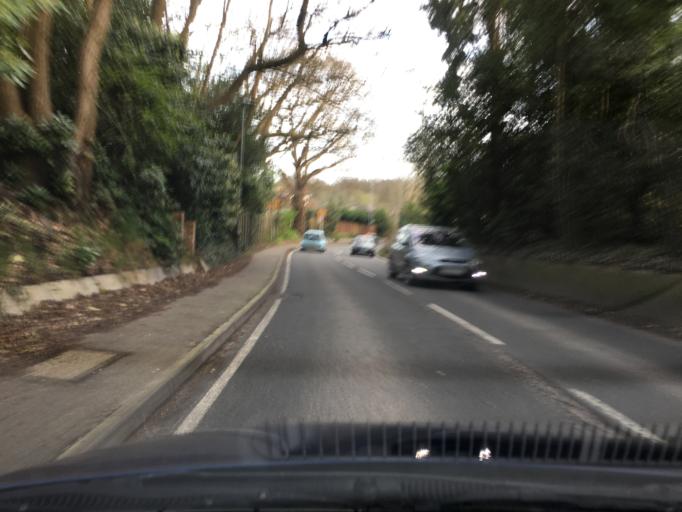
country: GB
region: England
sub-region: Hampshire
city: Yateley
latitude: 51.3504
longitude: -0.8142
